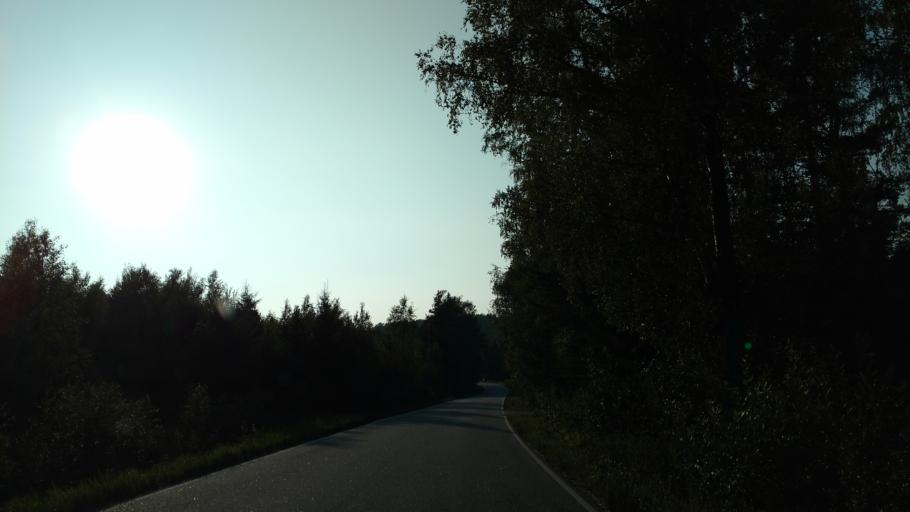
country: FI
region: Varsinais-Suomi
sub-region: Aboland-Turunmaa
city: Dragsfjaerd
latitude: 60.0300
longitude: 22.4488
